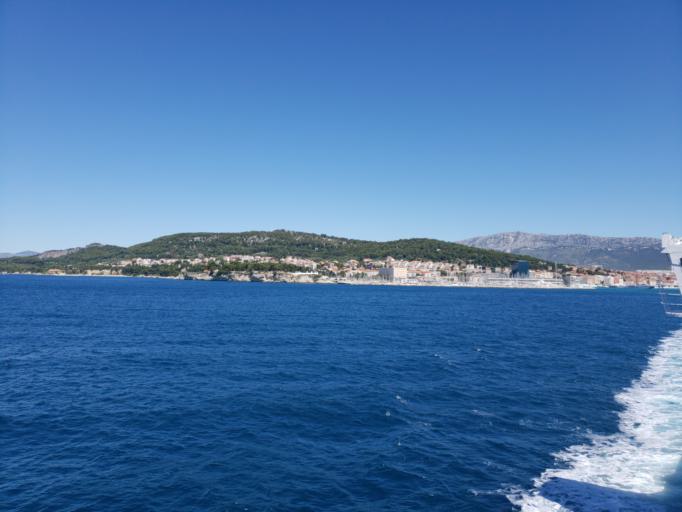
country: HR
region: Splitsko-Dalmatinska
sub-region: Grad Split
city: Split
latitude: 43.4950
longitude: 16.4338
